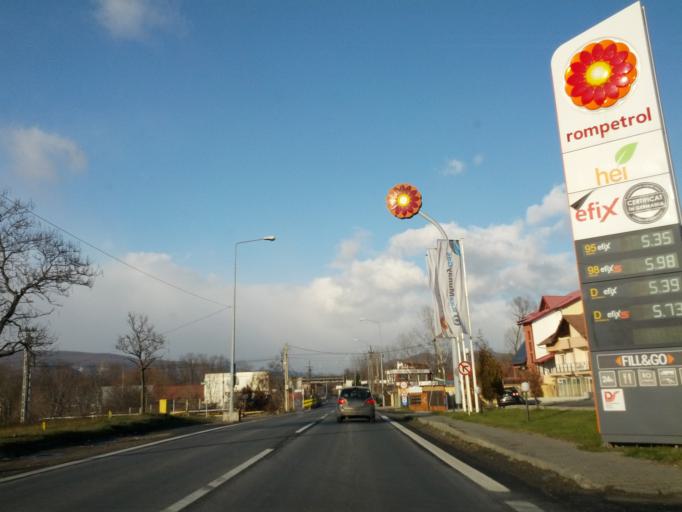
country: RO
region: Valcea
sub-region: Municipiul Ramnicu Valcea
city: Goranu
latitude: 45.1142
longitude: 24.3865
